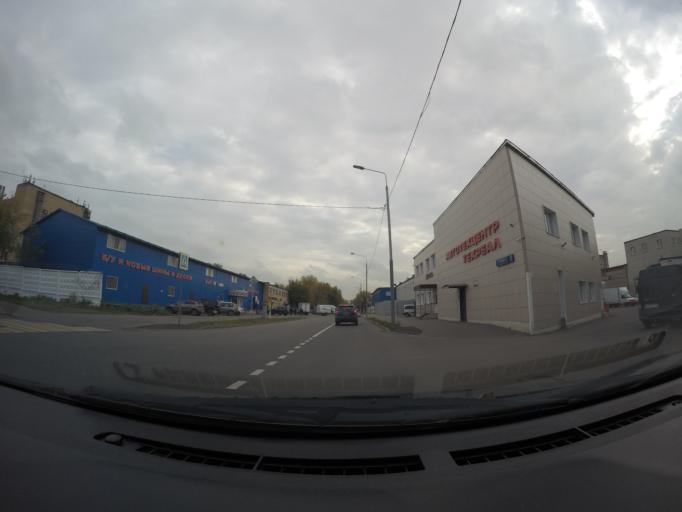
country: RU
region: Moscow
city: Lefortovo
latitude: 55.7595
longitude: 37.7327
